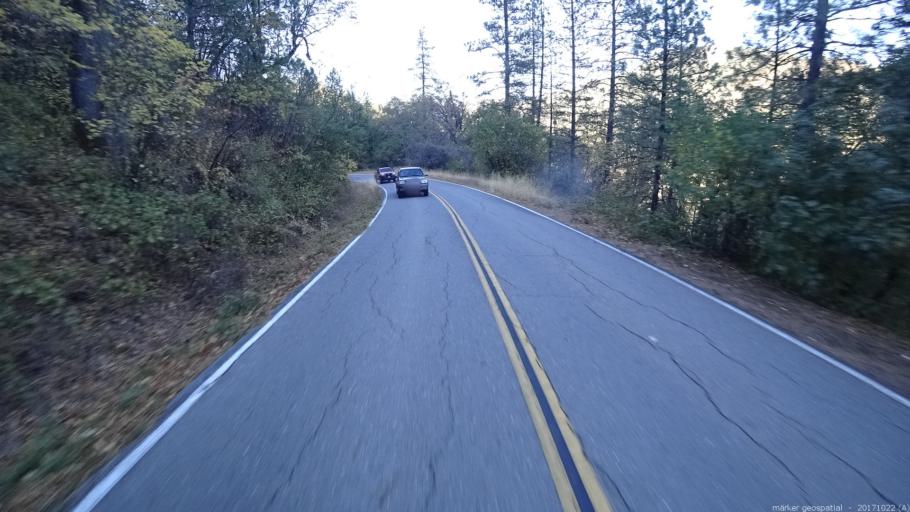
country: US
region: California
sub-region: Shasta County
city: Shasta Lake
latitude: 40.9052
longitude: -122.2358
